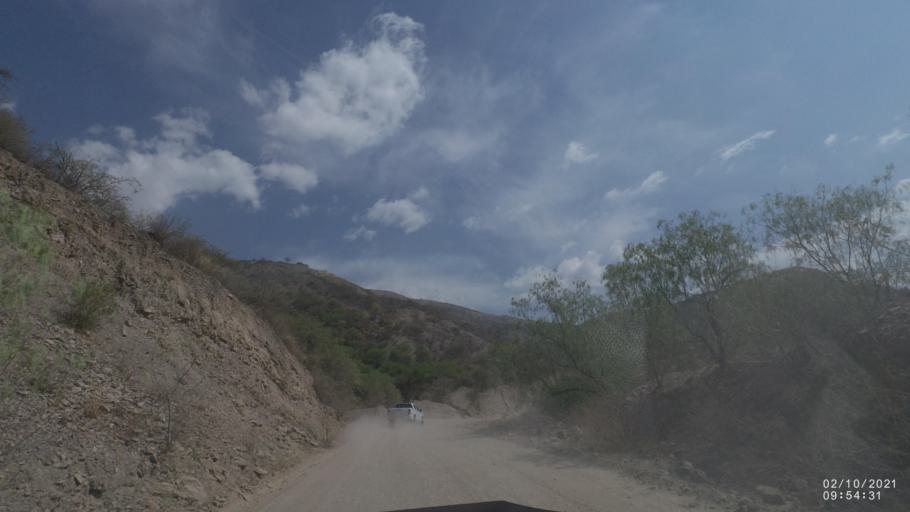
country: BO
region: Cochabamba
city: Irpa Irpa
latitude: -17.7963
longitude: -66.3503
